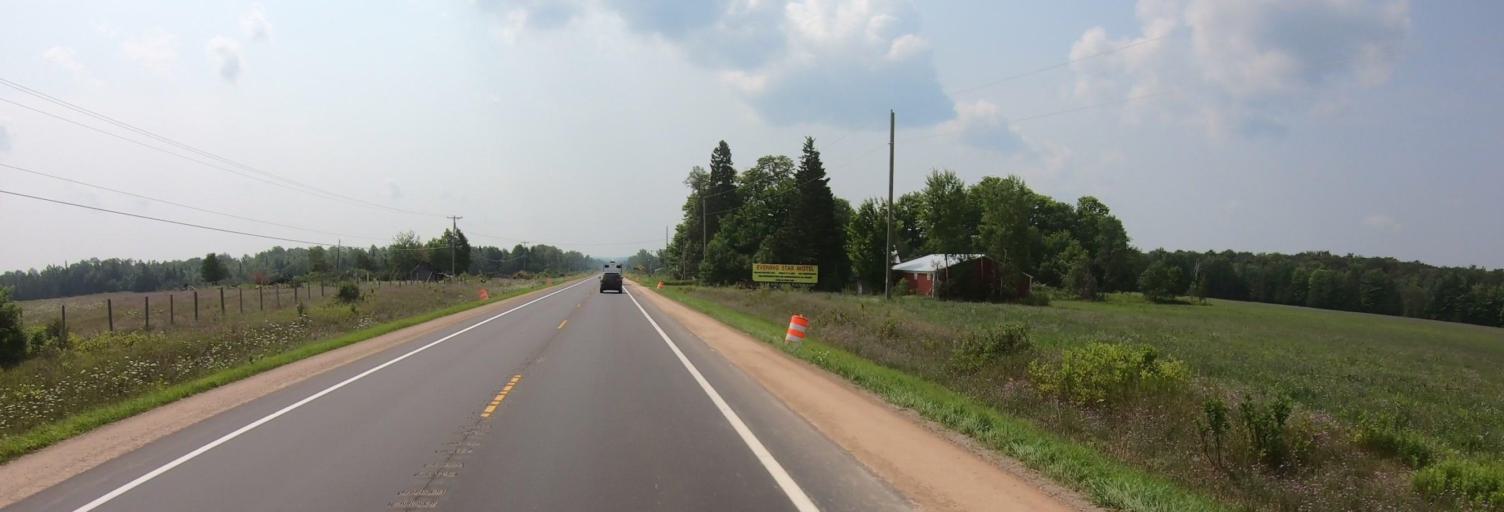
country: US
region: Michigan
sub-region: Luce County
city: Newberry
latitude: 46.4005
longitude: -85.5100
